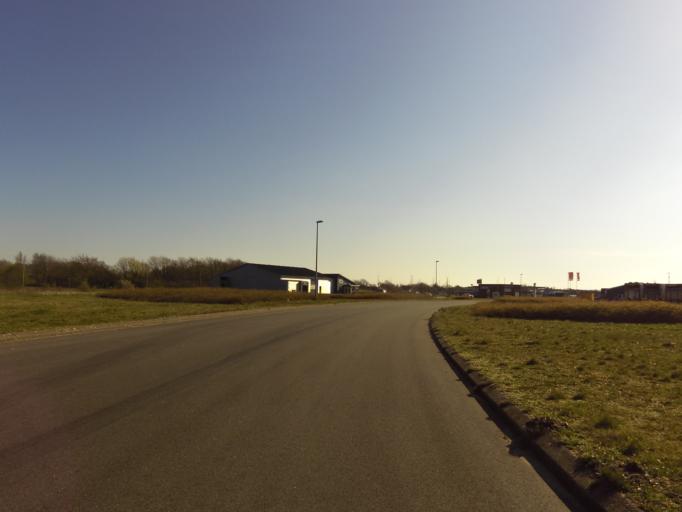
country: DK
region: South Denmark
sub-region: Esbjerg Kommune
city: Ribe
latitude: 55.3540
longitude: 8.7839
